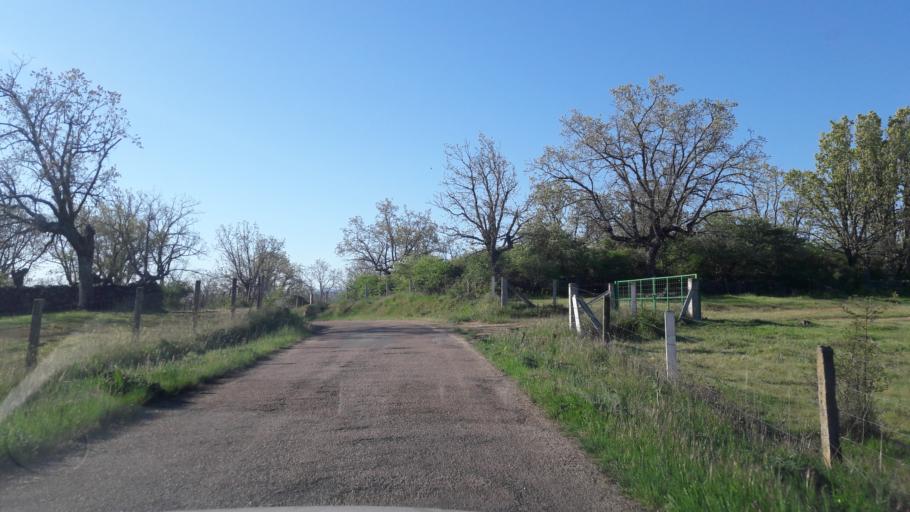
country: ES
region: Castille and Leon
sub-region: Provincia de Salamanca
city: Herguijuela del Campo
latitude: 40.6209
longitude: -5.8594
